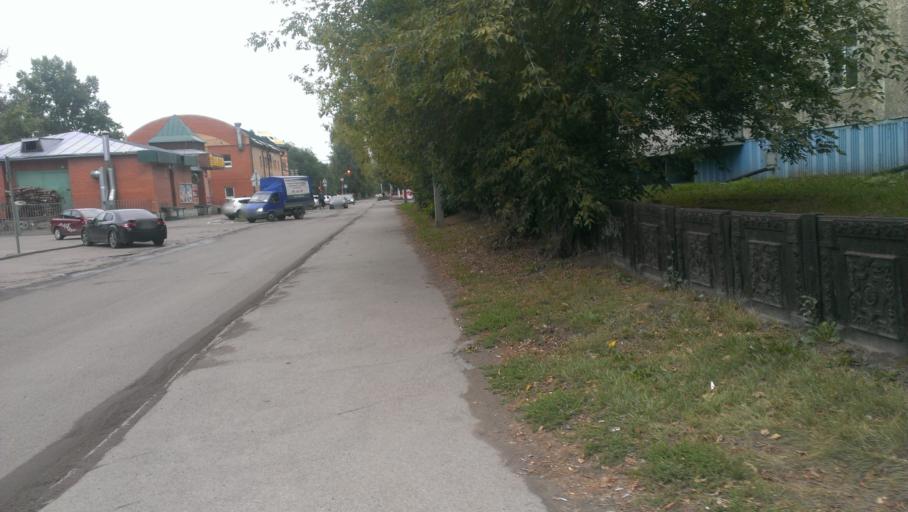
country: RU
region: Altai Krai
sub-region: Gorod Barnaulskiy
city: Barnaul
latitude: 53.3714
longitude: 83.6903
